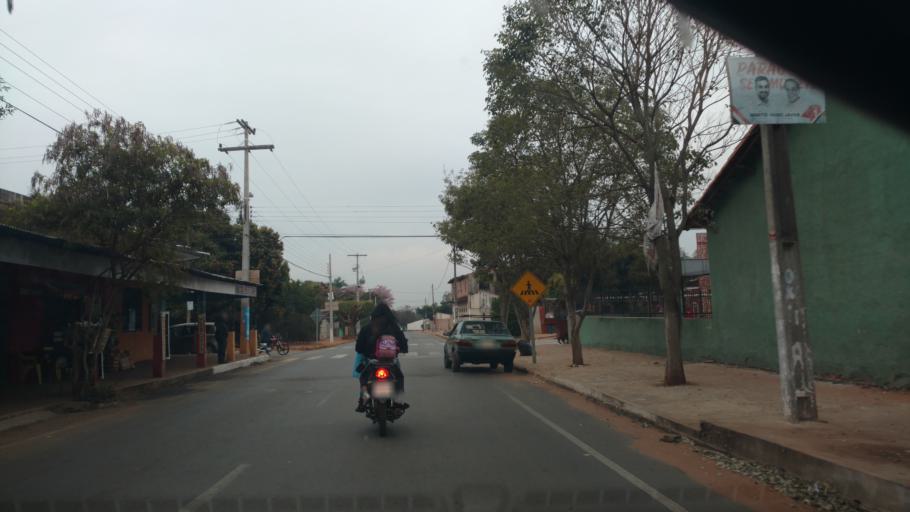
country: PY
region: Central
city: San Lorenzo
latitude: -25.3551
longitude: -57.4812
